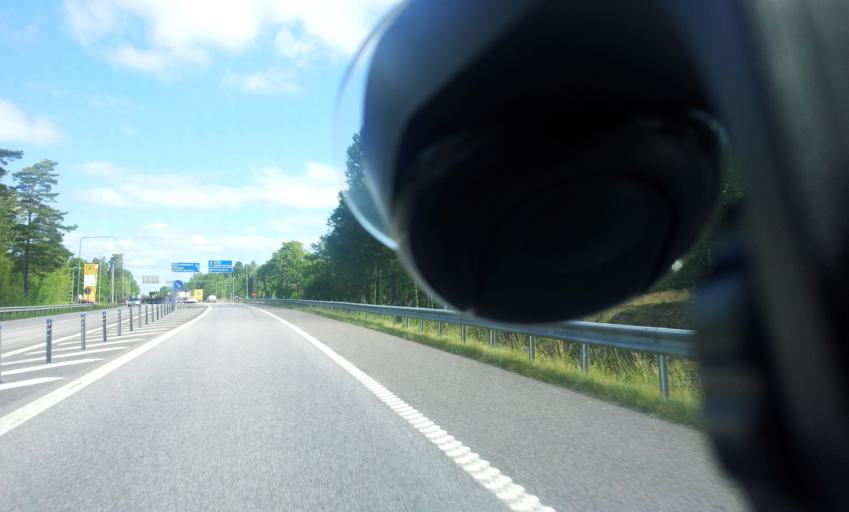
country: SE
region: Kalmar
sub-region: Monsteras Kommun
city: Timmernabben
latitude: 56.9424
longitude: 16.3894
